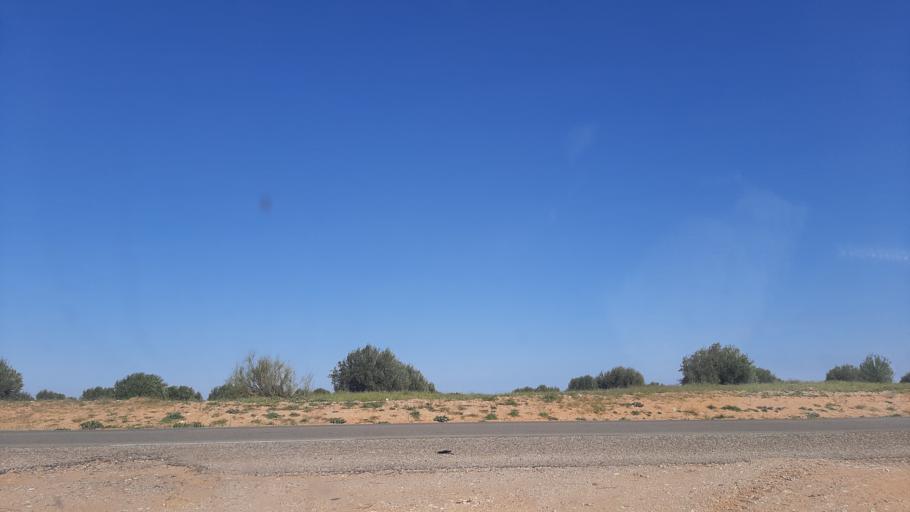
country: TN
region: Madanin
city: Medenine
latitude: 33.2859
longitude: 10.7874
